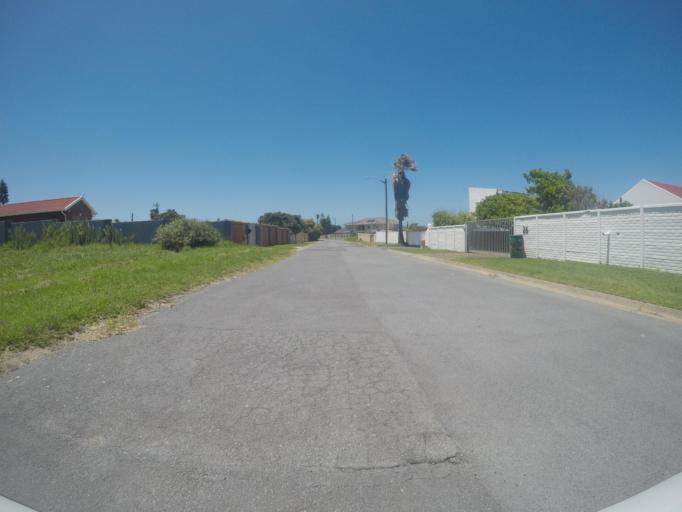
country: ZA
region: Eastern Cape
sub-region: Buffalo City Metropolitan Municipality
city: East London
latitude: -32.9539
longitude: 28.0065
